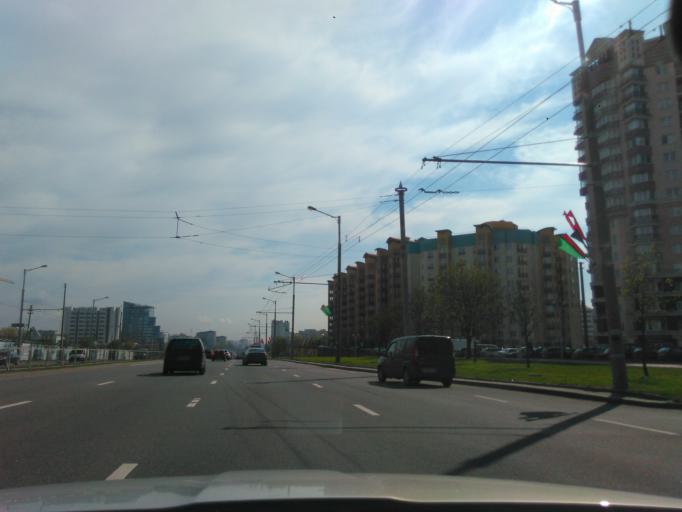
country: BY
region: Minsk
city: Novoye Medvezhino
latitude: 53.9064
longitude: 27.4574
